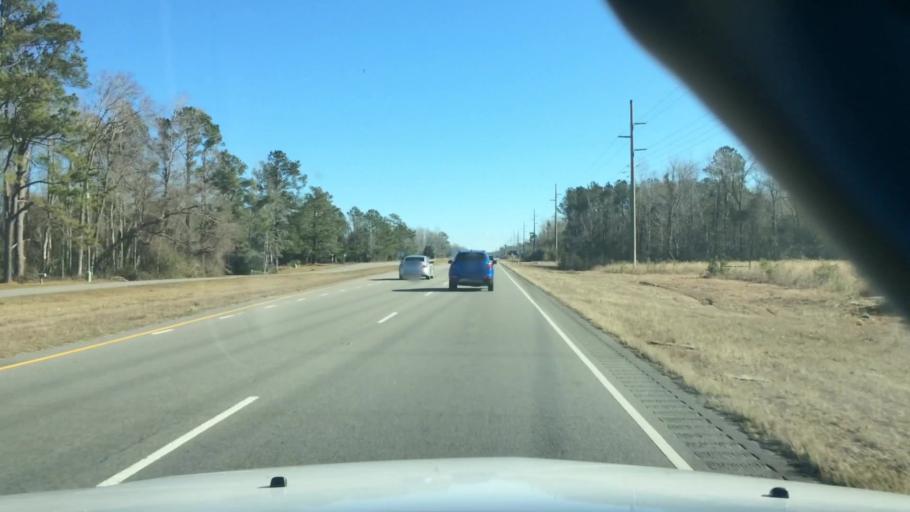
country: US
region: North Carolina
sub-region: Brunswick County
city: Shallotte
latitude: 34.0037
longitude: -78.3108
